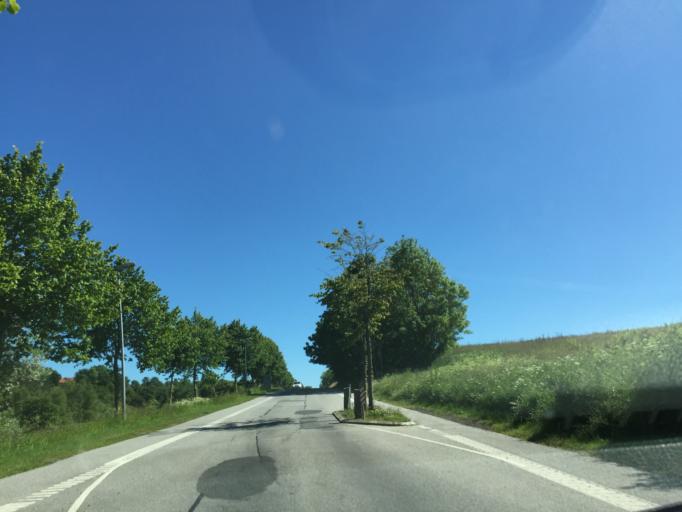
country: DK
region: Central Jutland
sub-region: Viborg Kommune
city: Bjerringbro
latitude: 56.3608
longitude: 9.6647
